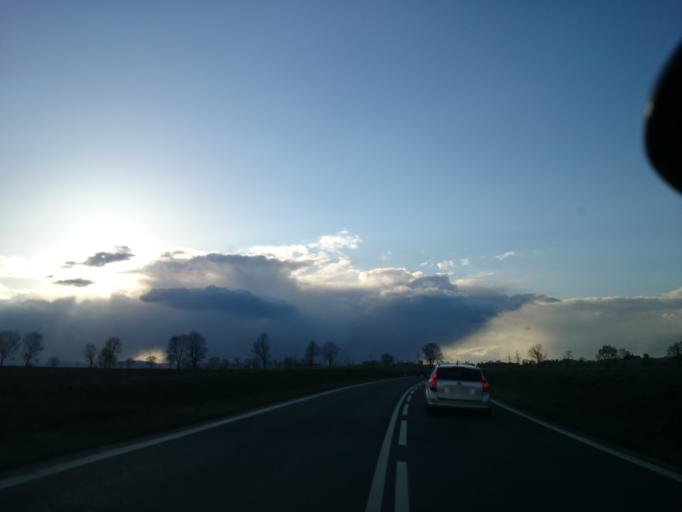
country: PL
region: Lower Silesian Voivodeship
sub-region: Powiat zabkowicki
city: Zabkowice Slaskie
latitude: 50.5717
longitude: 16.8259
